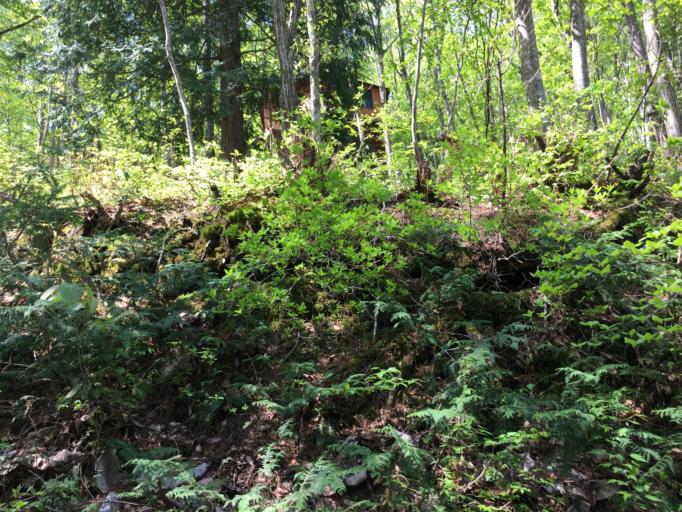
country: JP
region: Nagano
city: Omachi
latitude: 36.5090
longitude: 137.7963
